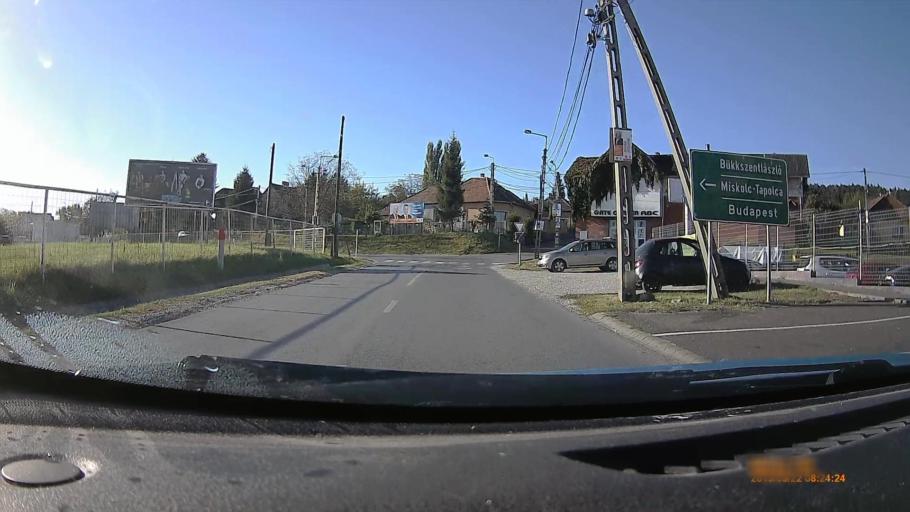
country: HU
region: Borsod-Abauj-Zemplen
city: Miskolc
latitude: 48.0908
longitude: 20.7113
